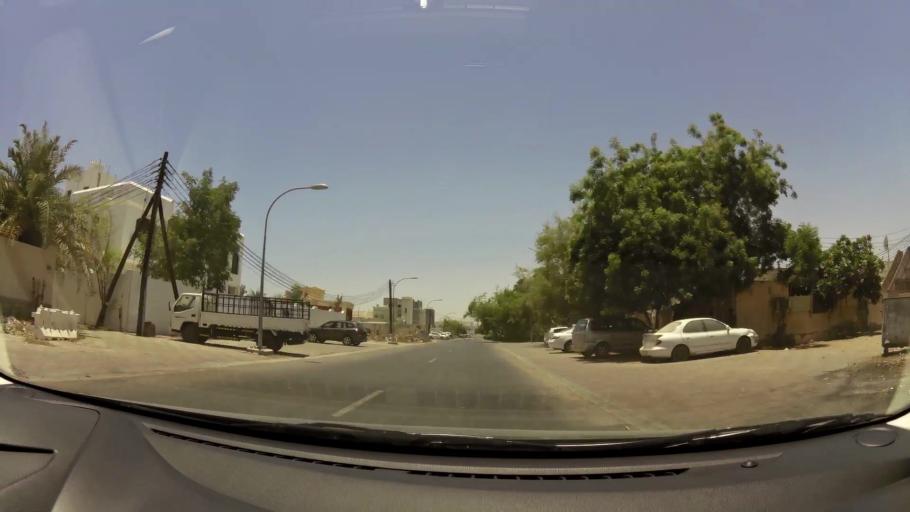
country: OM
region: Muhafazat Masqat
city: As Sib al Jadidah
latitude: 23.6352
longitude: 58.2324
